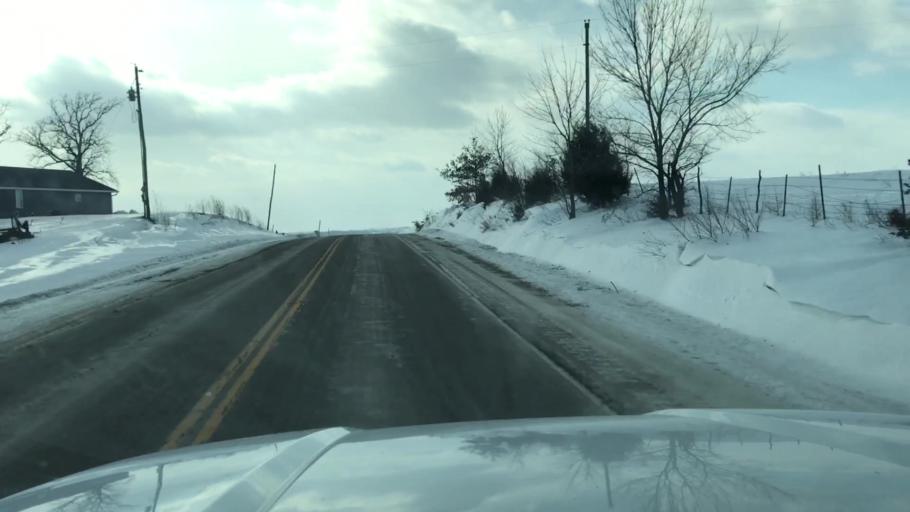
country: US
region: Missouri
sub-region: Gentry County
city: Stanberry
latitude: 40.3662
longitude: -94.6507
